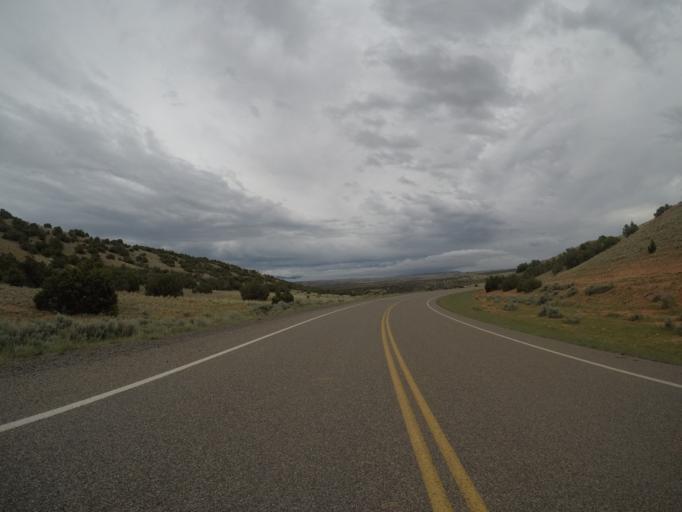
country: US
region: Wyoming
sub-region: Big Horn County
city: Lovell
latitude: 45.1044
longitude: -108.2379
